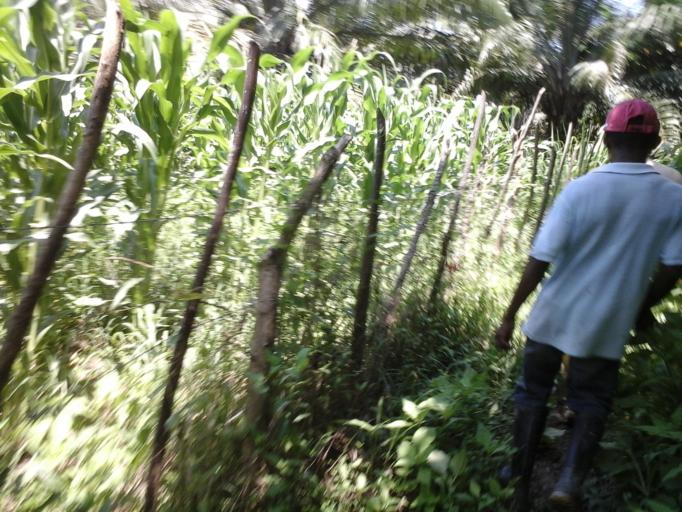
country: CO
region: Bolivar
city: San Pablo
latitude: 10.1608
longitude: -75.2734
